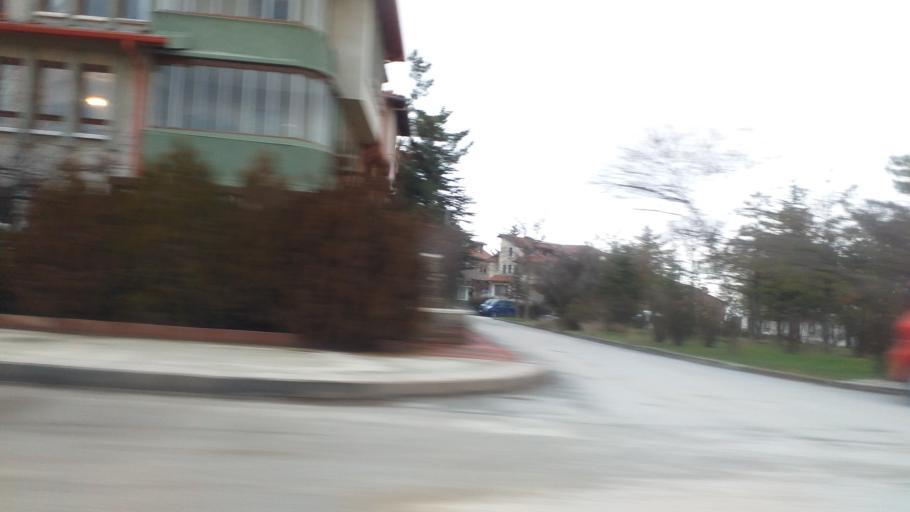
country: TR
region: Ankara
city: Batikent
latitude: 39.8919
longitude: 32.7238
